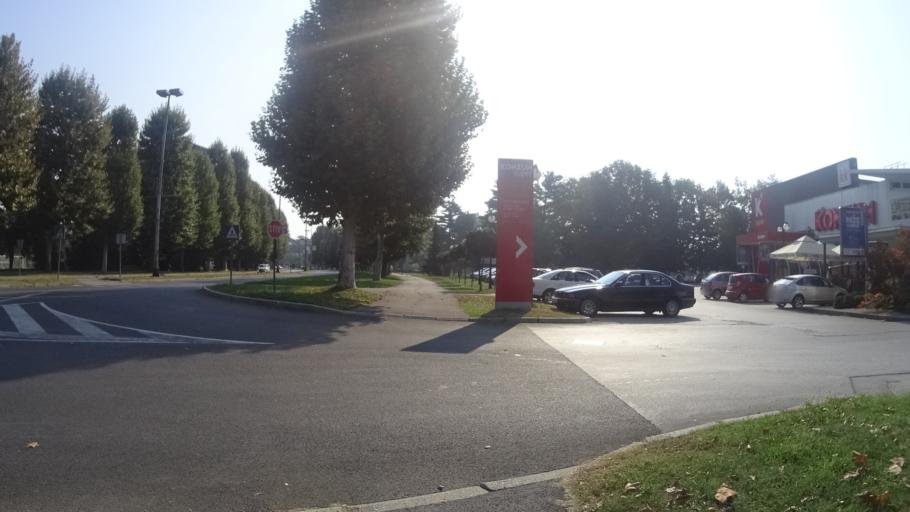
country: HR
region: Medimurska
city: Cakovec
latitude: 46.3871
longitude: 16.4238
